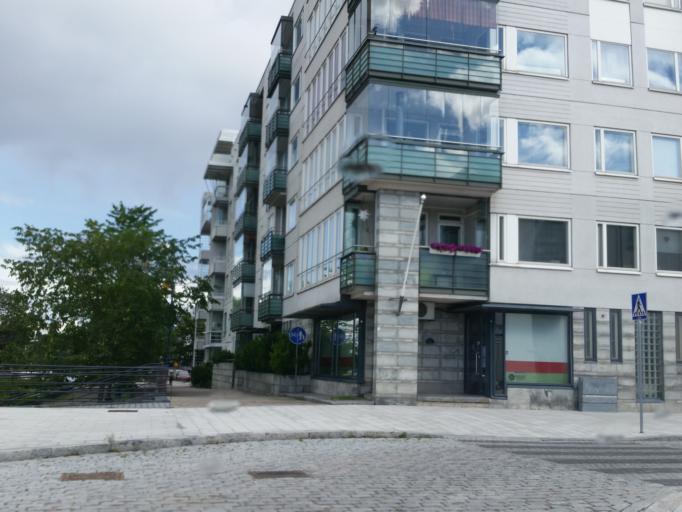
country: FI
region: Uusimaa
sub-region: Helsinki
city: Helsinki
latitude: 60.1601
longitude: 24.9102
